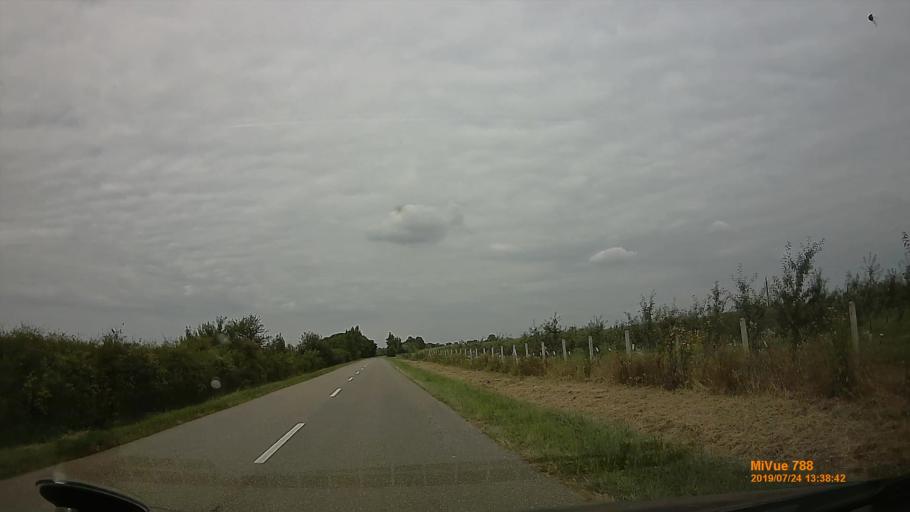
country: HU
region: Szabolcs-Szatmar-Bereg
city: Aranyosapati
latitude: 48.2302
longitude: 22.3208
